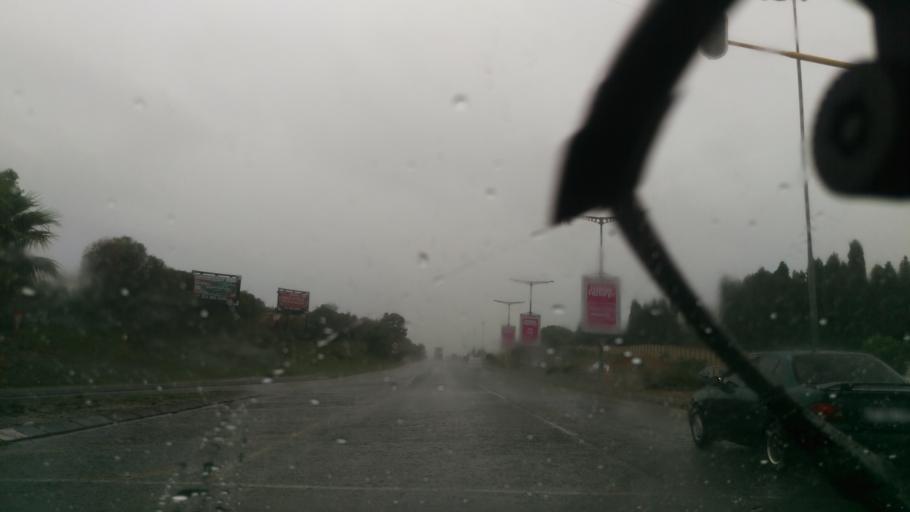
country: ZA
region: Gauteng
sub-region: West Rand District Municipality
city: Muldersdriseloop
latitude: -26.0638
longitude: 27.9415
